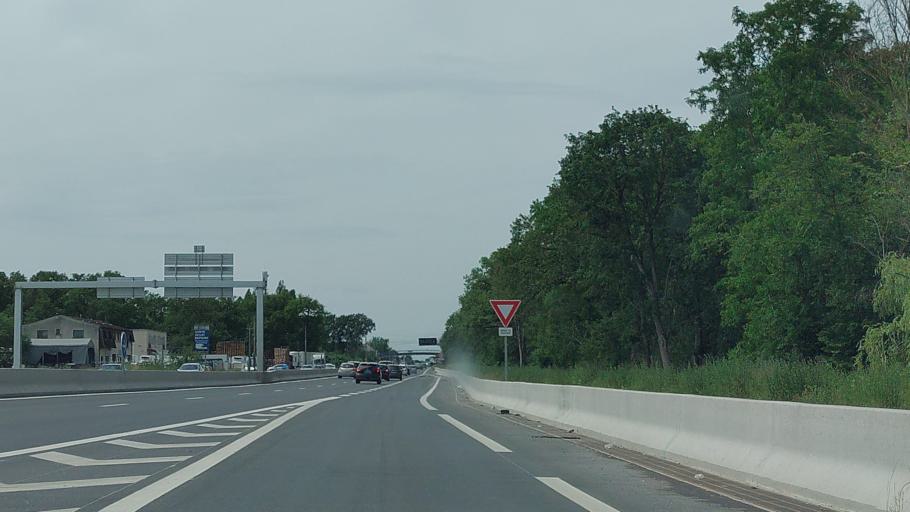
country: FR
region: Ile-de-France
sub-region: Departement de Seine-et-Marne
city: Villevaude
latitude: 48.9431
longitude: 2.6497
